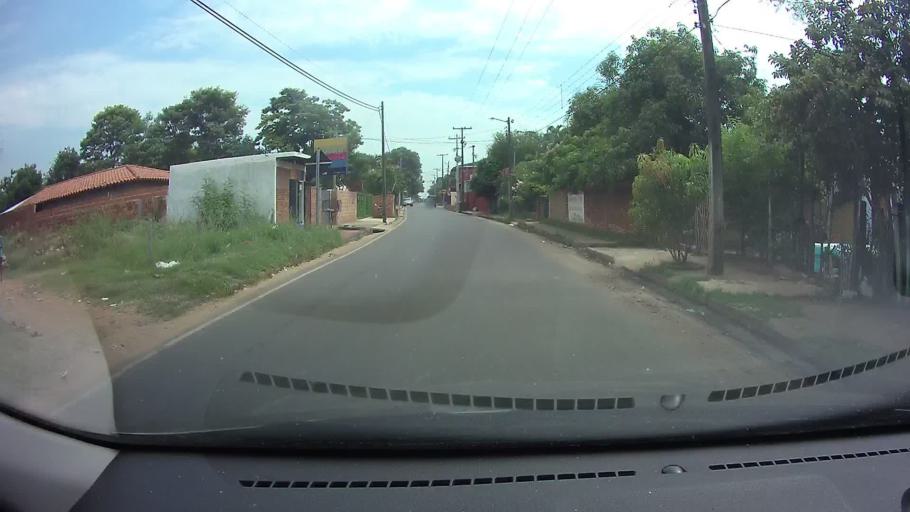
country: PY
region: Central
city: San Lorenzo
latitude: -25.2905
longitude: -57.5047
